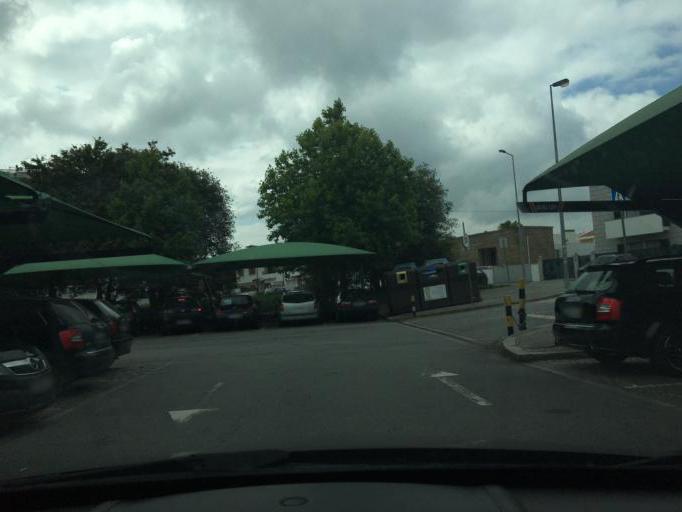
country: PT
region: Porto
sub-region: Maia
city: Gemunde
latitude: 41.2552
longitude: -8.6502
